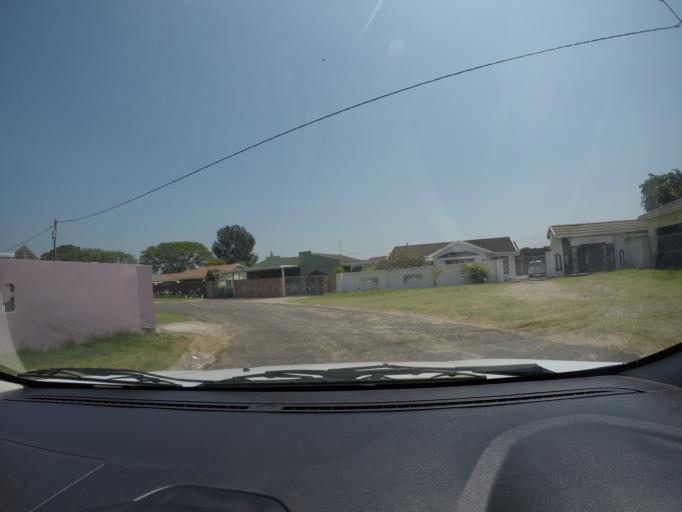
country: ZA
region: KwaZulu-Natal
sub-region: uThungulu District Municipality
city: eSikhawini
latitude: -28.8686
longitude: 31.9225
